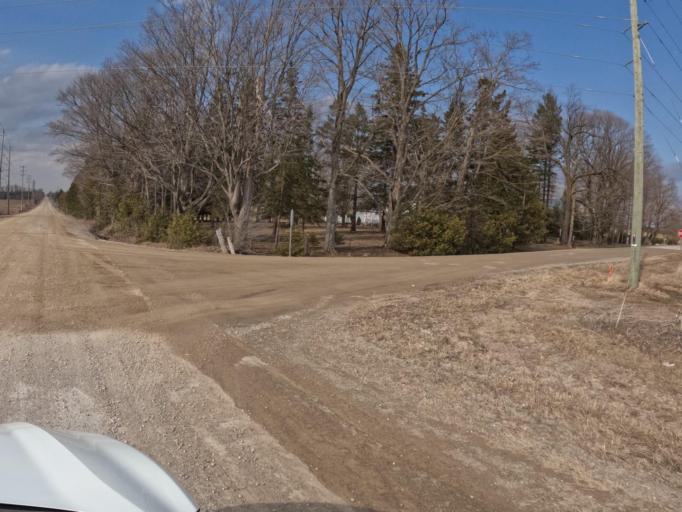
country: CA
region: Ontario
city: Shelburne
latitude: 43.9049
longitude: -80.3022
